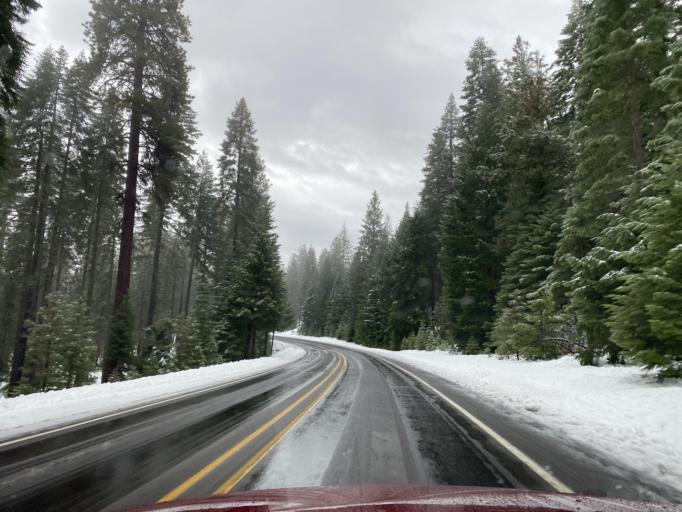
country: US
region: Oregon
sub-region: Klamath County
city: Klamath Falls
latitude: 42.5270
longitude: -122.0891
